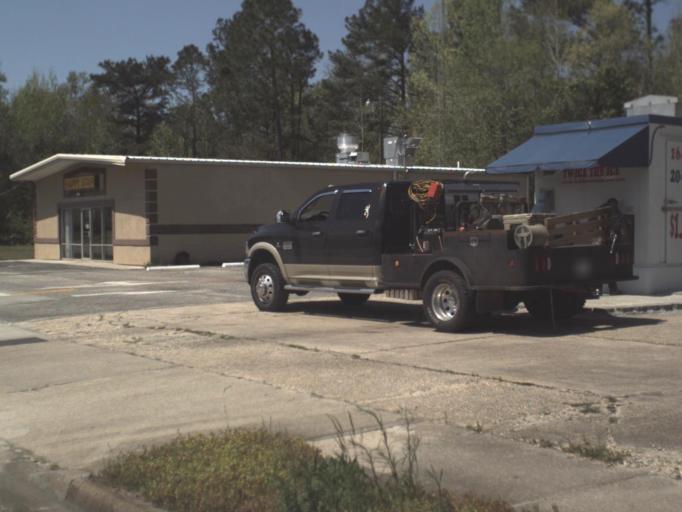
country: US
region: Florida
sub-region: Escambia County
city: Century
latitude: 30.9804
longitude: -87.2584
